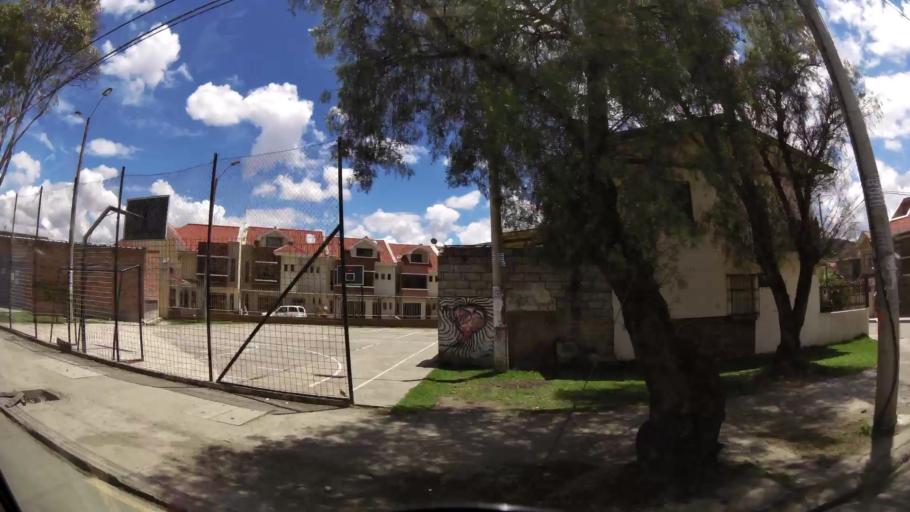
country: EC
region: Azuay
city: Cuenca
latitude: -2.9199
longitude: -79.0389
